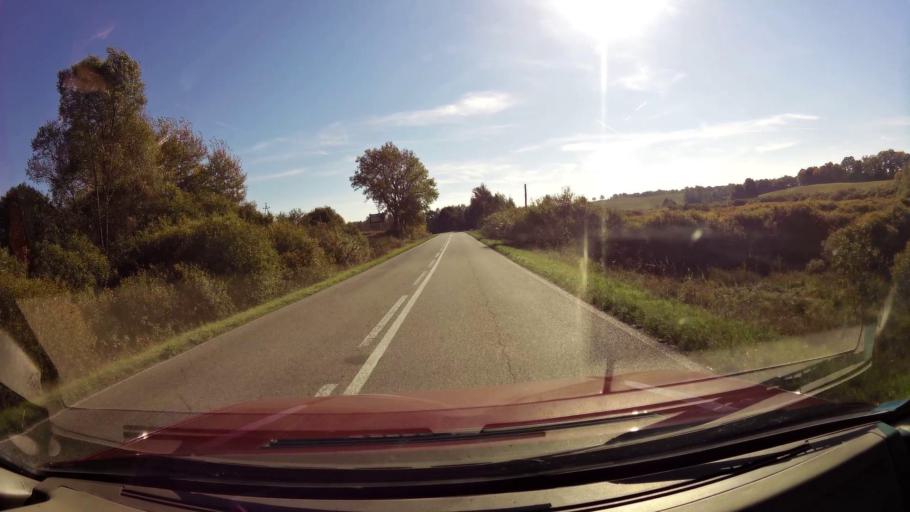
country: PL
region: West Pomeranian Voivodeship
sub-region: Powiat swidwinski
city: Polczyn-Zdroj
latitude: 53.7210
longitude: 16.1124
